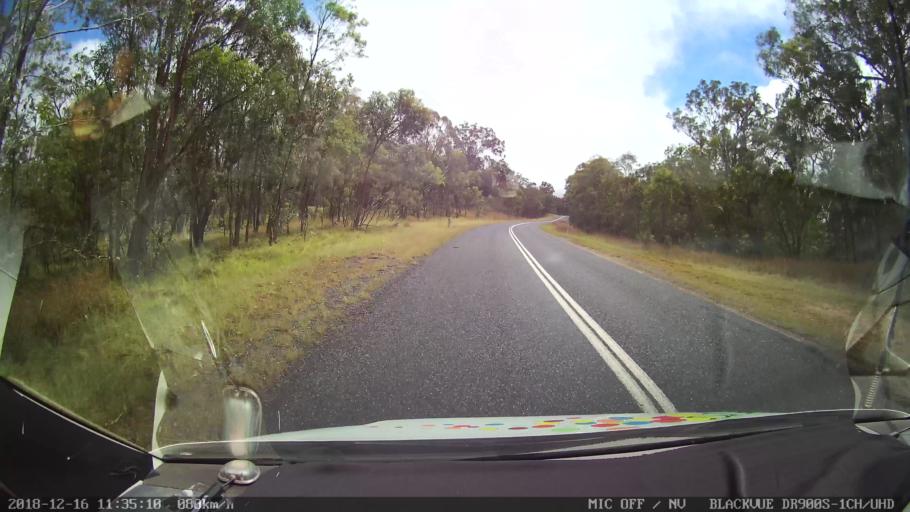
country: AU
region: New South Wales
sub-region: Tenterfield Municipality
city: Carrolls Creek
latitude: -28.9928
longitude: 152.1604
